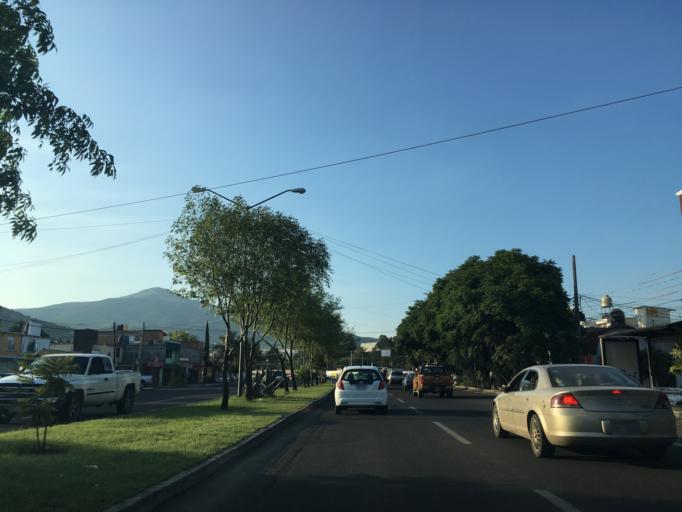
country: MX
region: Michoacan
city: Morelia
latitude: 19.7120
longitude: -101.2269
